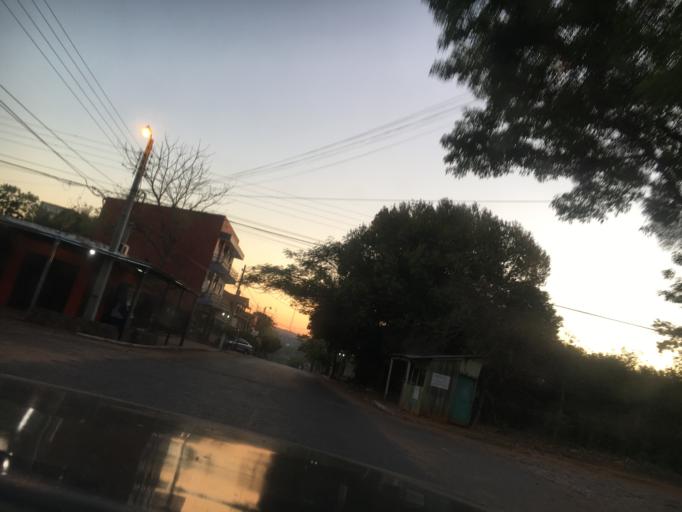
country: PY
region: Central
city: Villa Elisa
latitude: -25.3652
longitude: -57.5841
